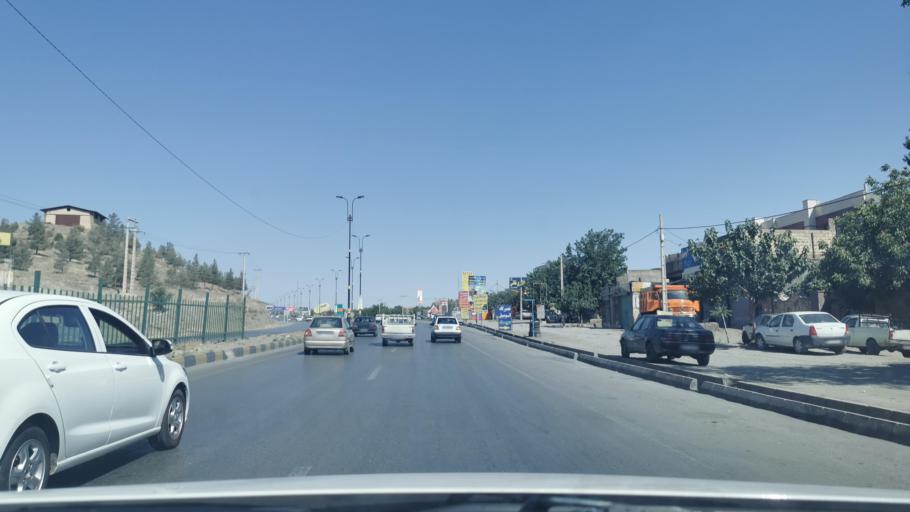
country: IR
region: Razavi Khorasan
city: Torqabeh
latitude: 36.4016
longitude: 59.3879
